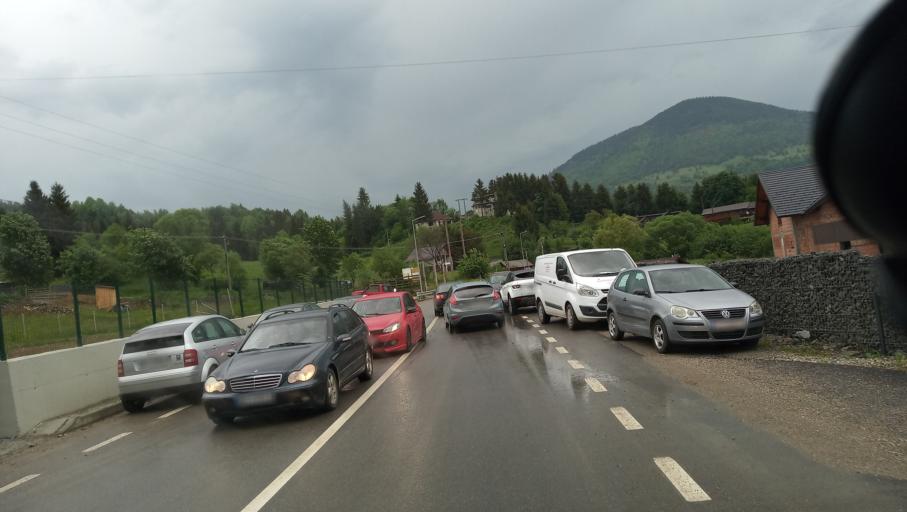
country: RO
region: Bistrita-Nasaud
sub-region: Comuna Tiha Bargaului
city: Tureac
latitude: 47.1703
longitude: 24.8868
